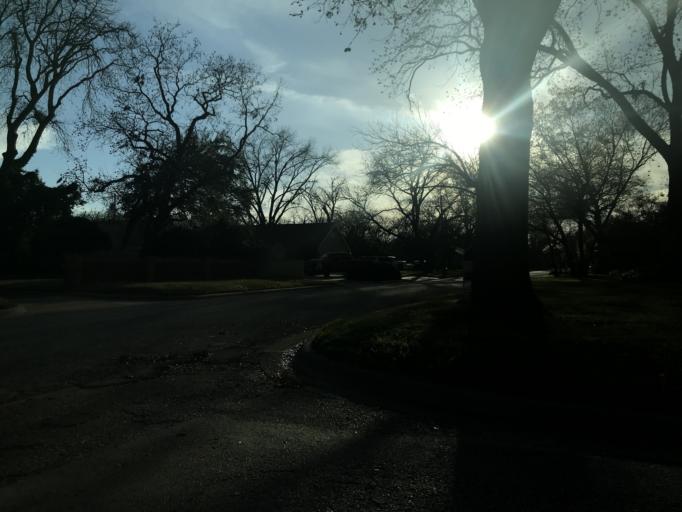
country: US
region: Texas
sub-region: Taylor County
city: Abilene
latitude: 32.4359
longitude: -99.7675
